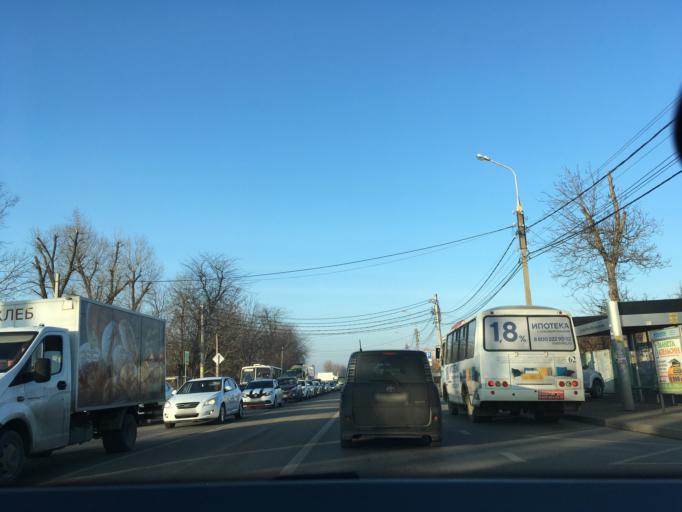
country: RU
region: Krasnodarskiy
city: Krasnodar
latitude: 45.0955
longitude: 39.0137
